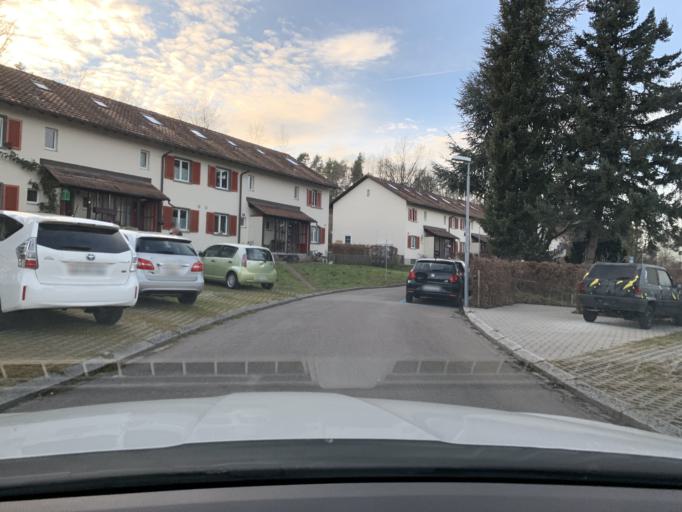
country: CH
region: Zurich
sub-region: Bezirk Zuerich
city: Zuerich (Kreis 12) / Hirzenbach
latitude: 47.3966
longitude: 8.5938
